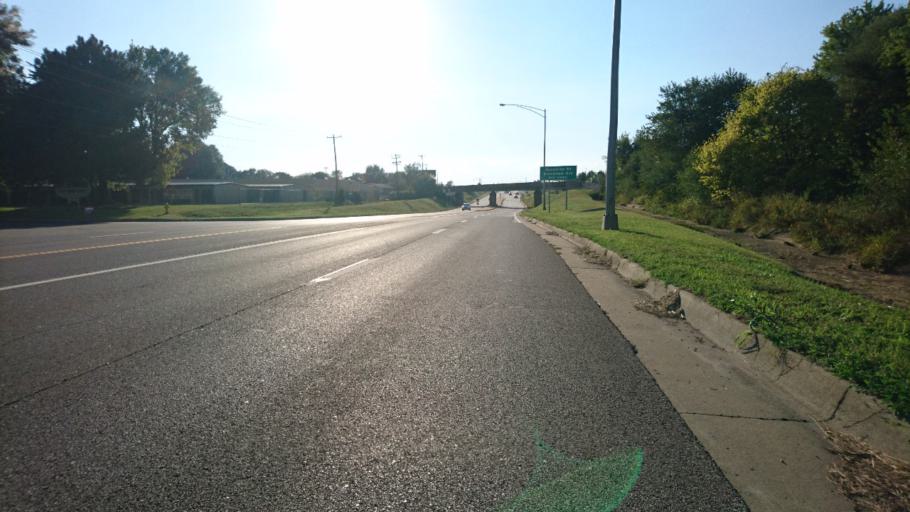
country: US
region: Missouri
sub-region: Greene County
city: Springfield
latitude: 37.2126
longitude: -93.3764
